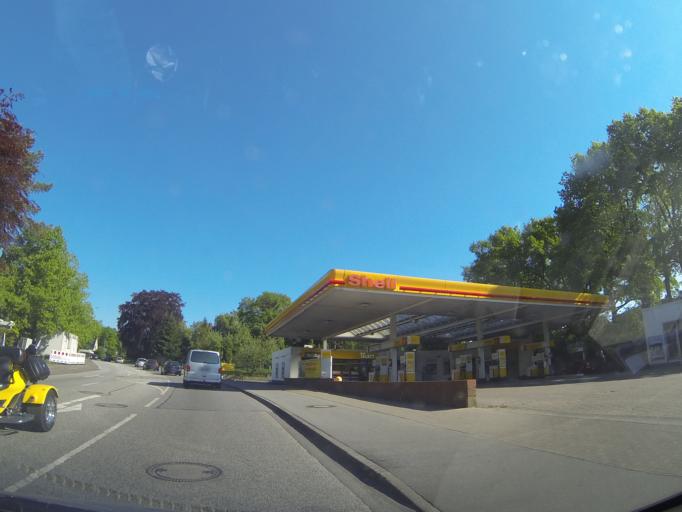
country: DE
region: Schleswig-Holstein
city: Halstenbek
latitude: 53.6317
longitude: 9.8375
